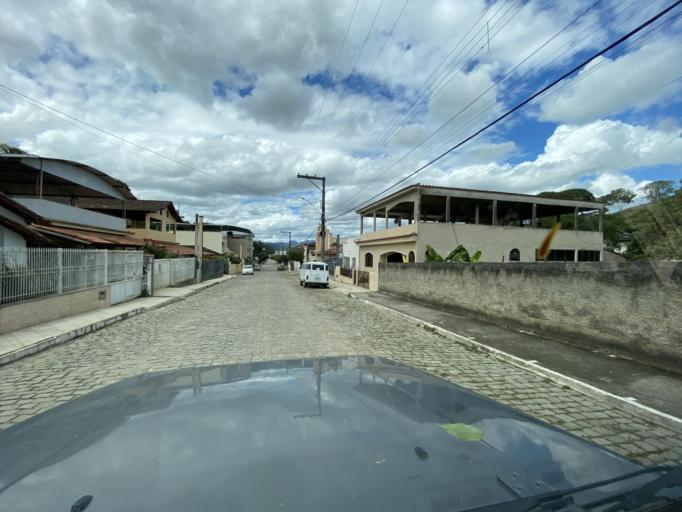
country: BR
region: Espirito Santo
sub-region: Jeronimo Monteiro
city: Jeronimo Monteiro
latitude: -20.7879
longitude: -41.3908
